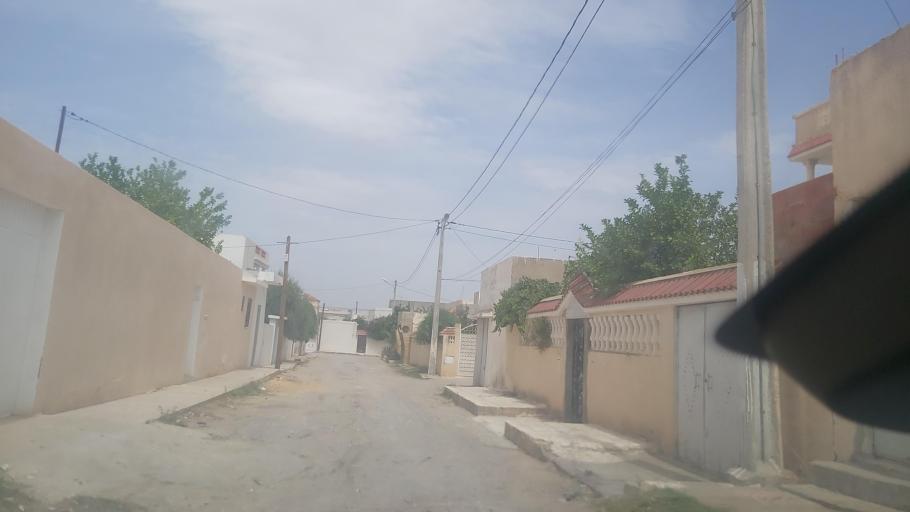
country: TN
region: Silyanah
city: Bu `Aradah
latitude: 36.3510
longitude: 9.6189
